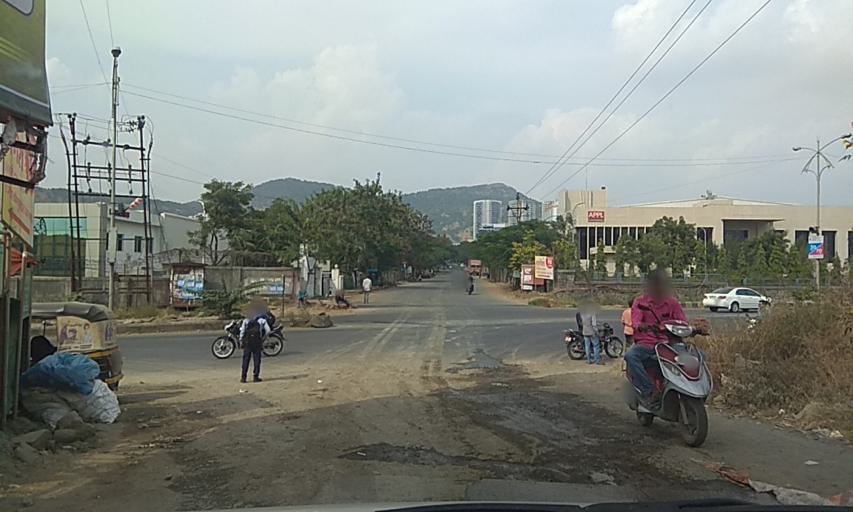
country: IN
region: Maharashtra
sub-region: Pune Division
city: Pimpri
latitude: 18.5888
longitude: 73.7053
